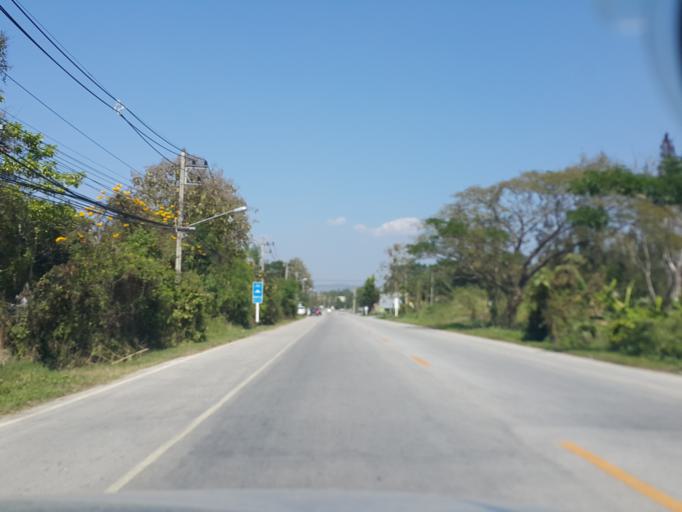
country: TH
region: Chiang Mai
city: San Sai
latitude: 18.8541
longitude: 99.1315
